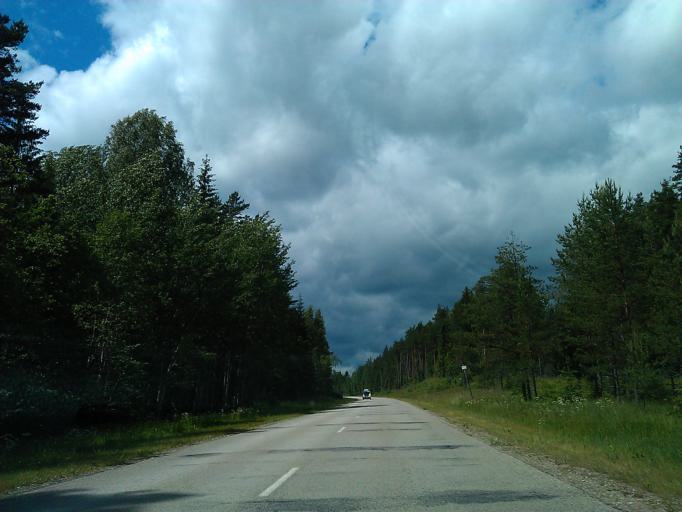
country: LV
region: Talsu Rajons
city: Stende
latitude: 57.0866
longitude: 22.5134
